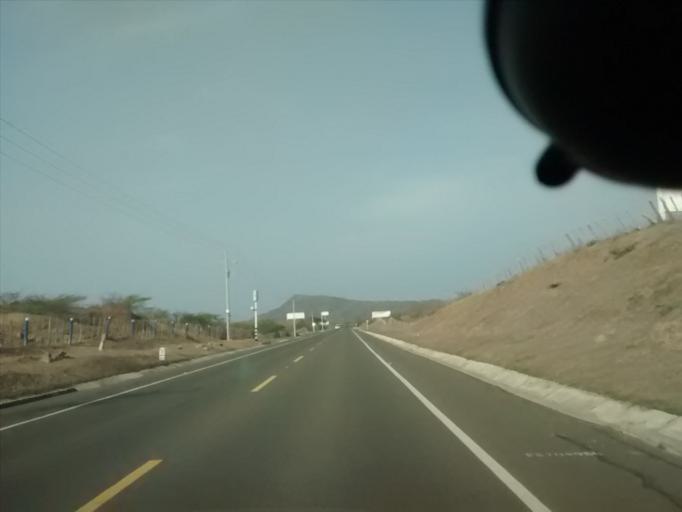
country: CO
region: Atlantico
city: Juan de Acosta
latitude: 10.8640
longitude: -75.1004
